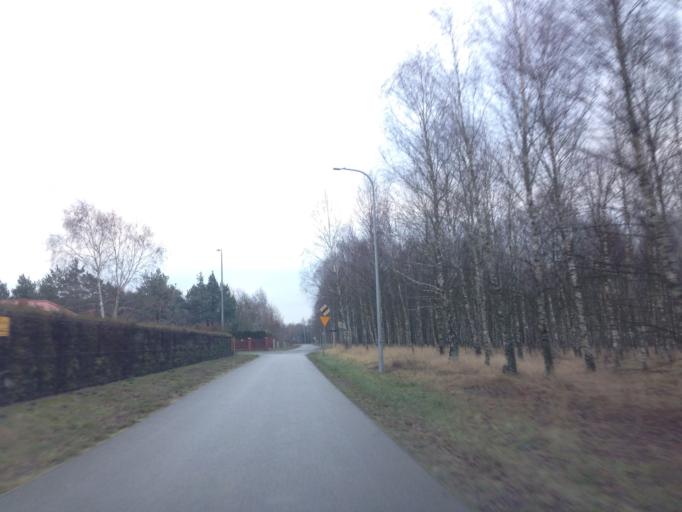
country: PL
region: Kujawsko-Pomorskie
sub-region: Powiat torunski
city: Wielka Nieszawka
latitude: 52.9889
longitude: 18.4443
